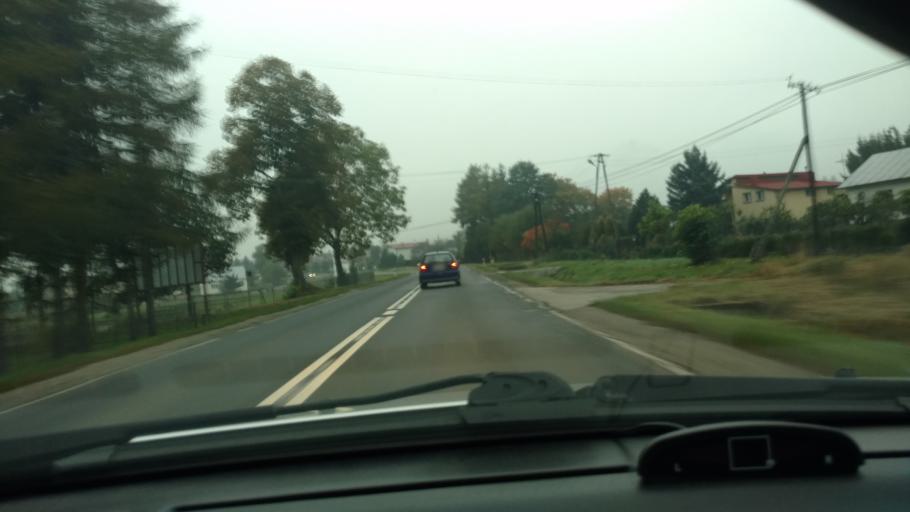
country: PL
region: Subcarpathian Voivodeship
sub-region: Powiat strzyzowski
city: Strzyzow
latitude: 49.8754
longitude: 21.7595
